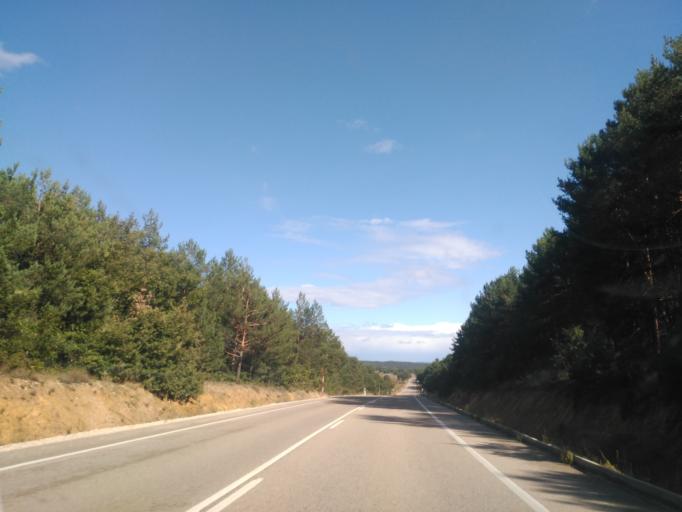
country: ES
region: Castille and Leon
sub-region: Provincia de Burgos
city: Cabezon de la Sierra
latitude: 41.8886
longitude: -3.2439
